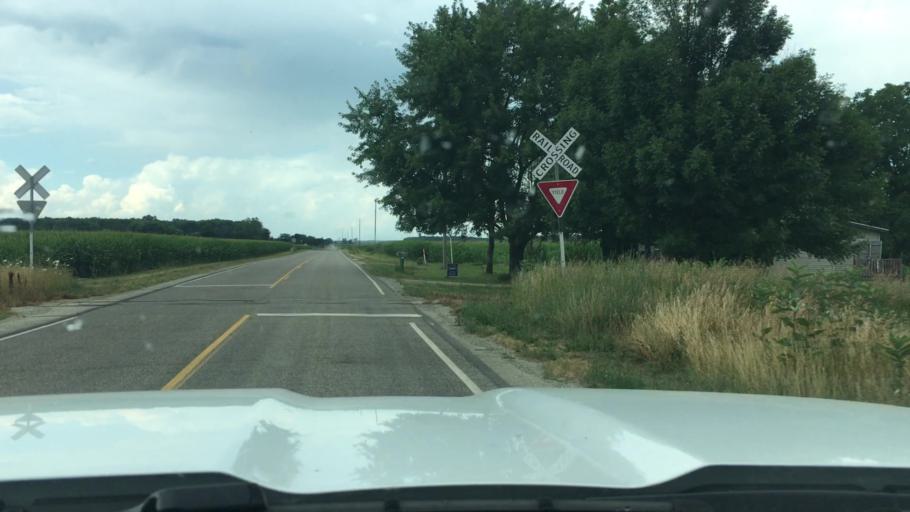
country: US
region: Michigan
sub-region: Montcalm County
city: Carson City
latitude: 43.1836
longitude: -84.7780
